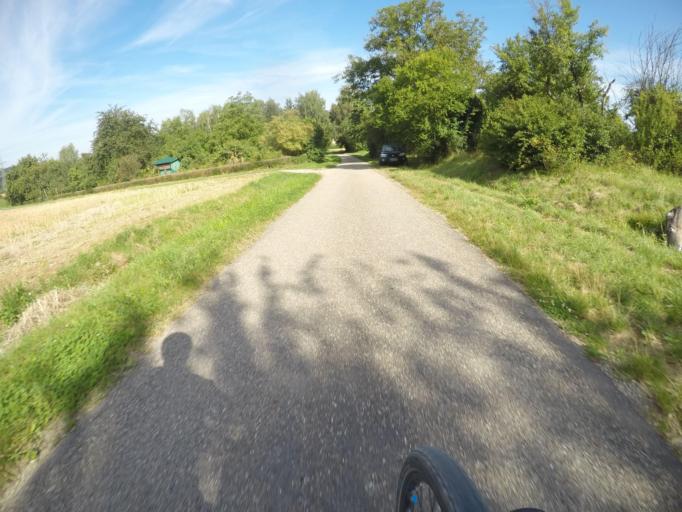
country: DE
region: Baden-Wuerttemberg
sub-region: Karlsruhe Region
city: Muhlacker
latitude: 48.9274
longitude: 8.8421
